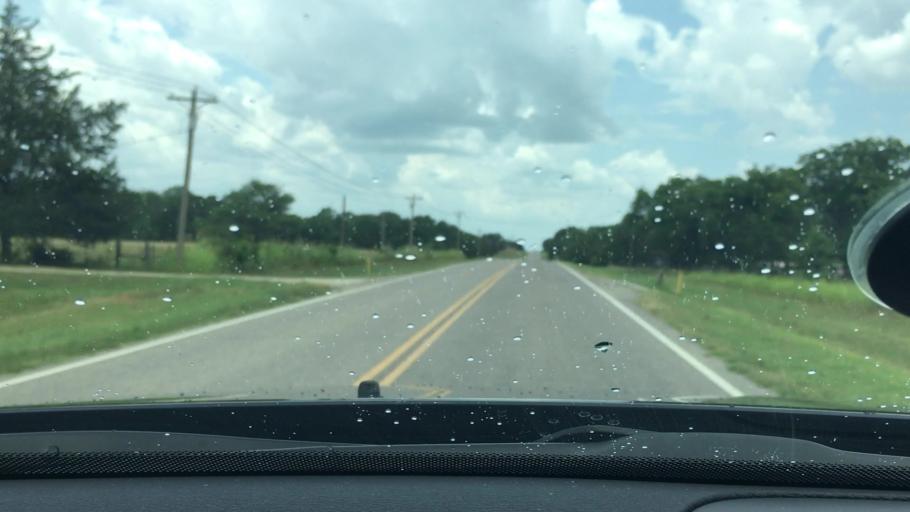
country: US
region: Oklahoma
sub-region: Love County
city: Marietta
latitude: 33.9490
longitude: -97.0340
